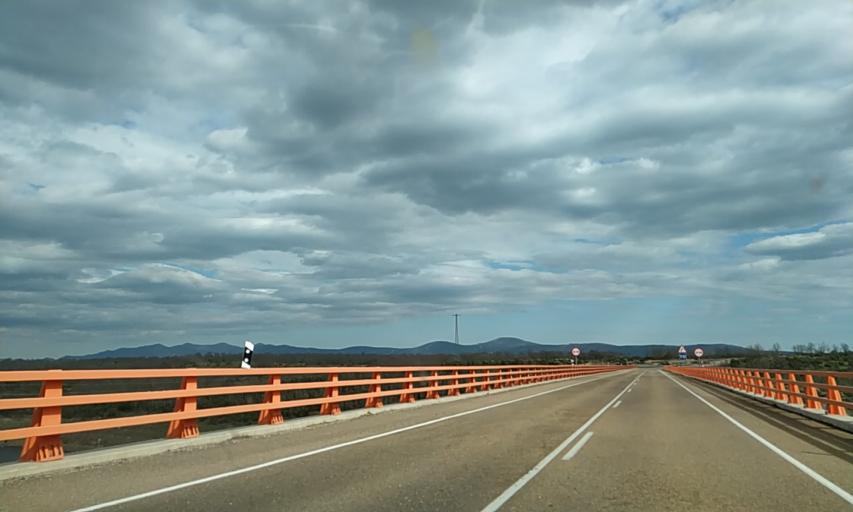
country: ES
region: Castille and Leon
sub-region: Provincia de Salamanca
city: Robleda
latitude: 40.4301
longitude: -6.6024
